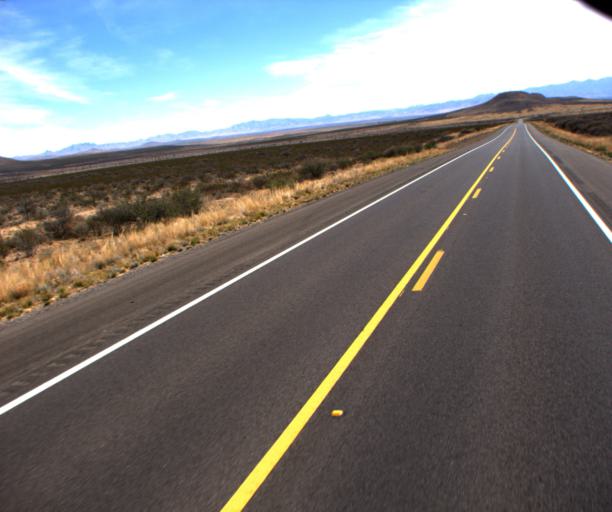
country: US
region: Arizona
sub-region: Cochise County
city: Willcox
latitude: 31.9056
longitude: -109.7432
